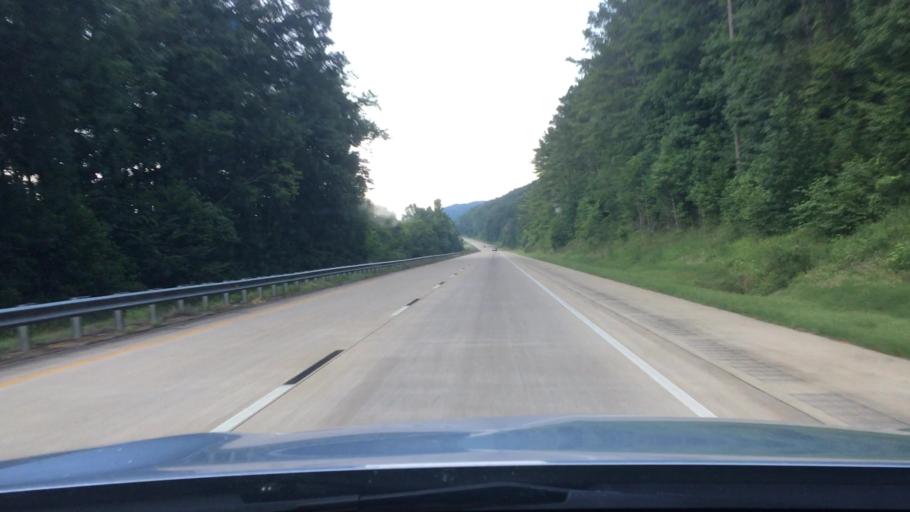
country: US
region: Alabama
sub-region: Etowah County
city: Gadsden
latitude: 34.1016
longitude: -86.0008
